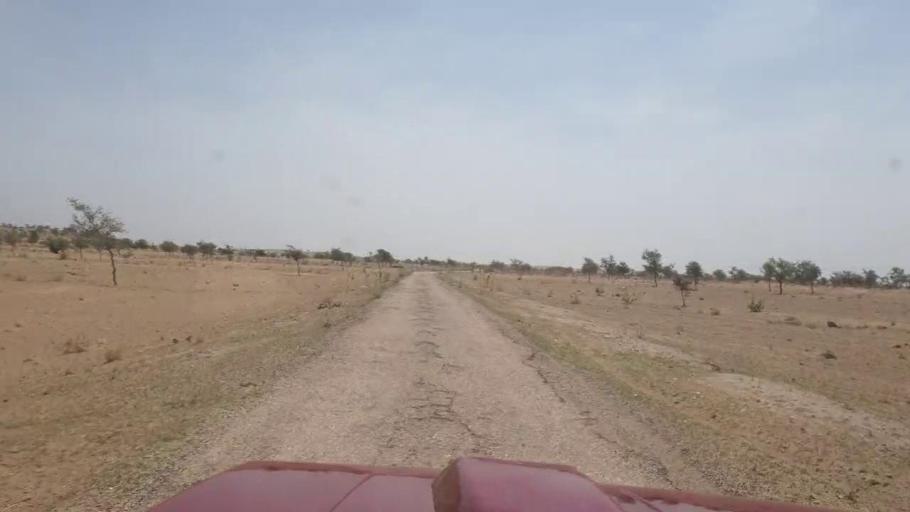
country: PK
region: Sindh
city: Islamkot
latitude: 25.1363
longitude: 70.3908
